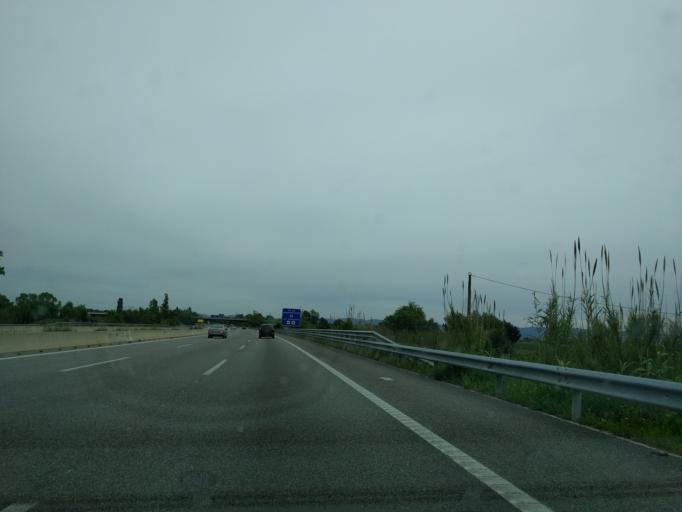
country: ES
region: Catalonia
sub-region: Provincia de Girona
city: Vilobi d'Onyar
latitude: 41.8790
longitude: 2.7680
